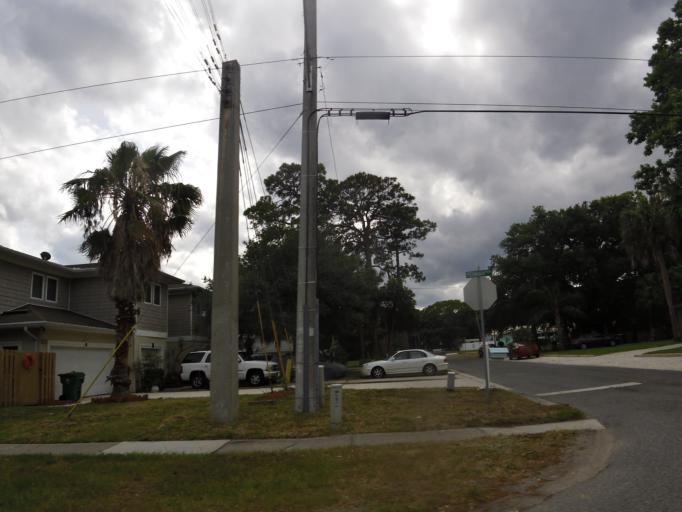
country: US
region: Florida
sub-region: Duval County
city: Jacksonville Beach
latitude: 30.2915
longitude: -81.4061
